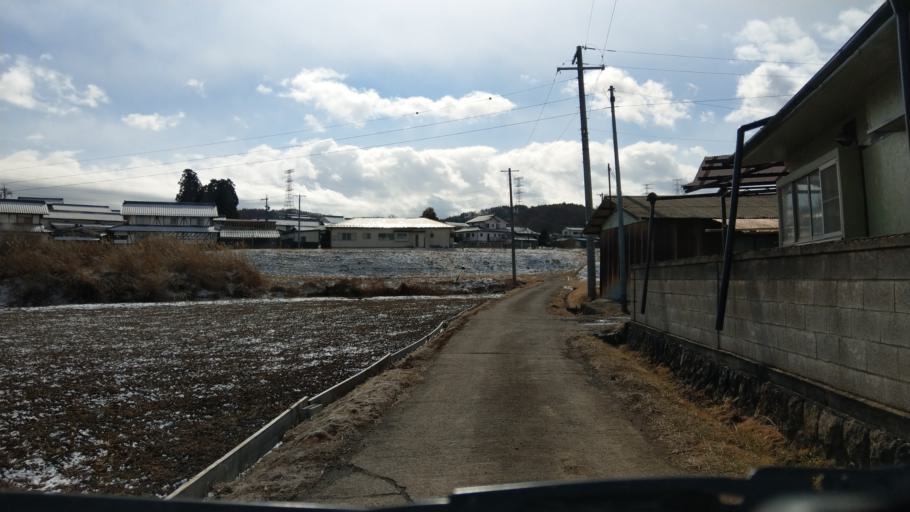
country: JP
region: Nagano
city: Kamimaruko
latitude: 36.2749
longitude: 138.3365
